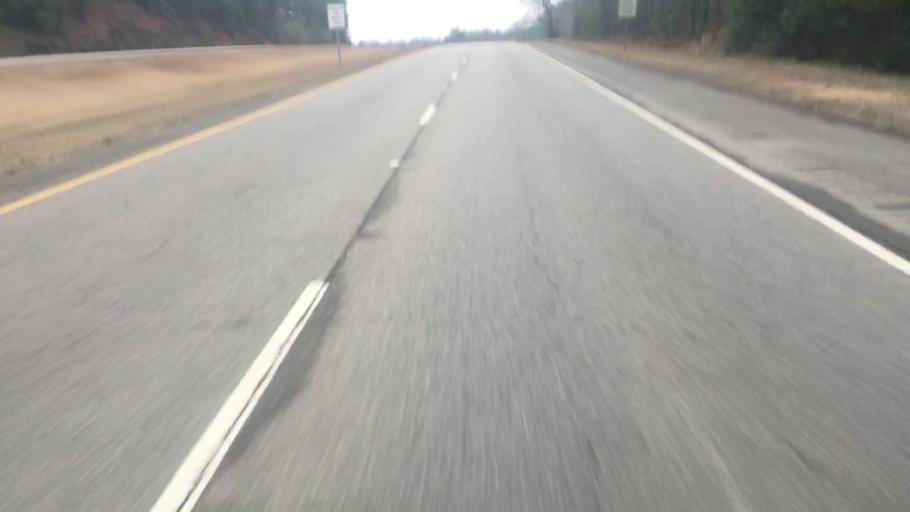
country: US
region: Alabama
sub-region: Walker County
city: Sumiton
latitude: 33.7660
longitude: -87.0702
